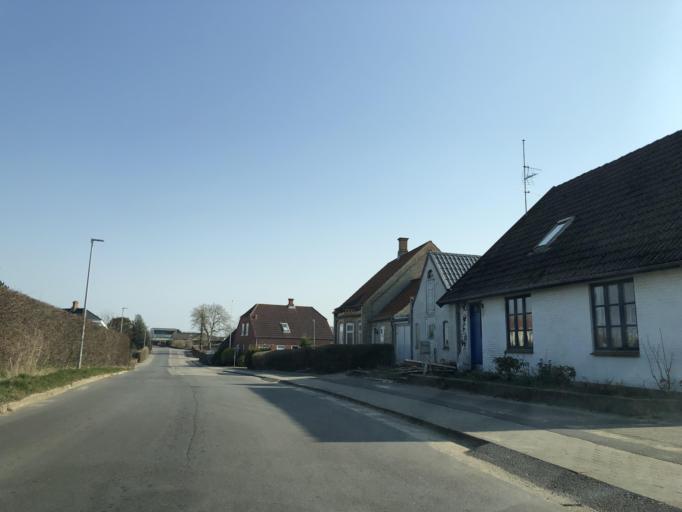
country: DK
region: South Denmark
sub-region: Sonderborg Kommune
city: Nordborg
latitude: 55.0616
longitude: 9.7400
